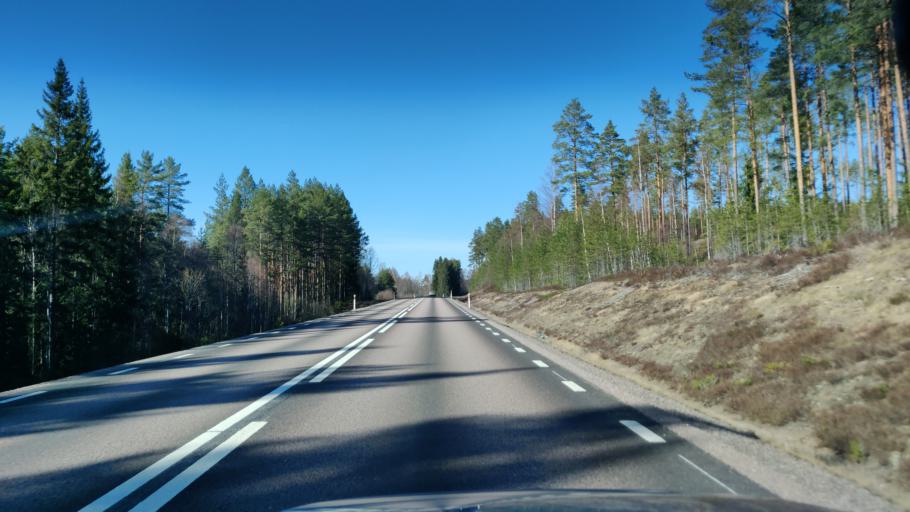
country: SE
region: Vaermland
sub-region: Hagfors Kommun
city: Hagfors
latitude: 59.9262
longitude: 13.6751
